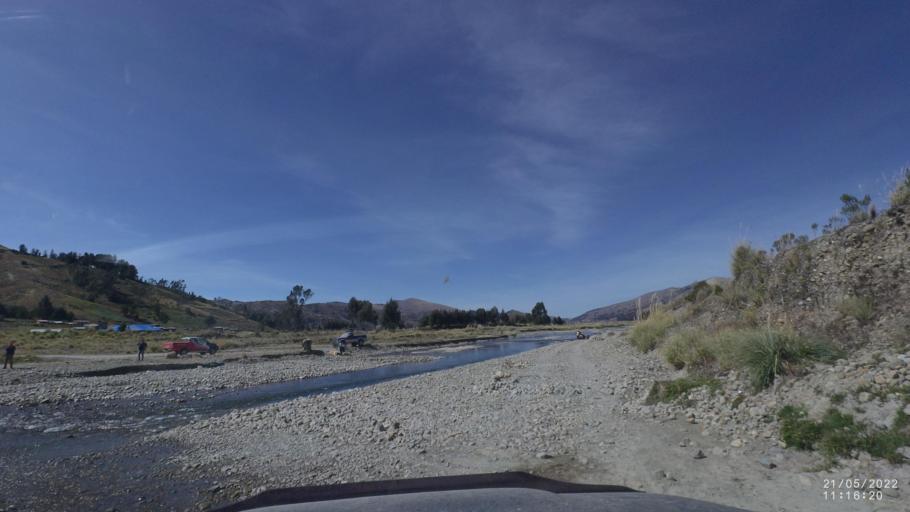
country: BO
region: Cochabamba
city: Colomi
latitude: -17.2758
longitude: -65.9219
